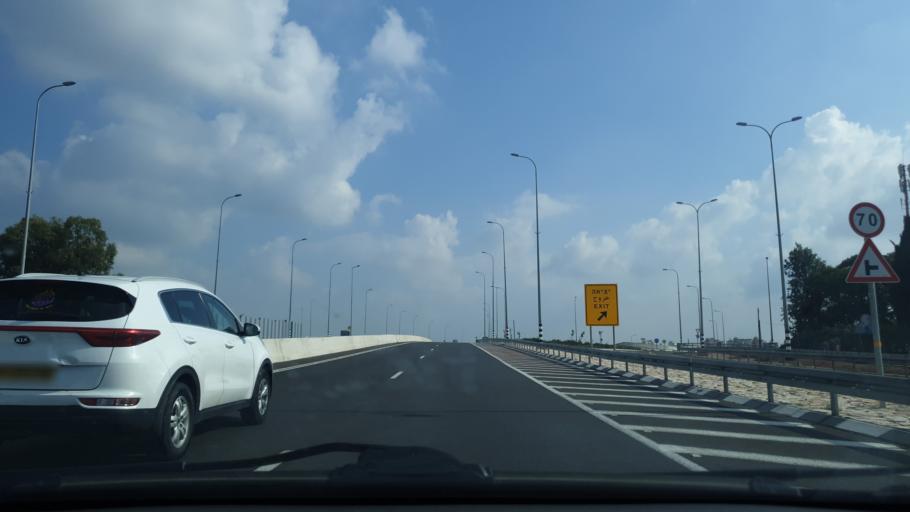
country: IL
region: Central District
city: Ramla
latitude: 31.9449
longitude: 34.8615
